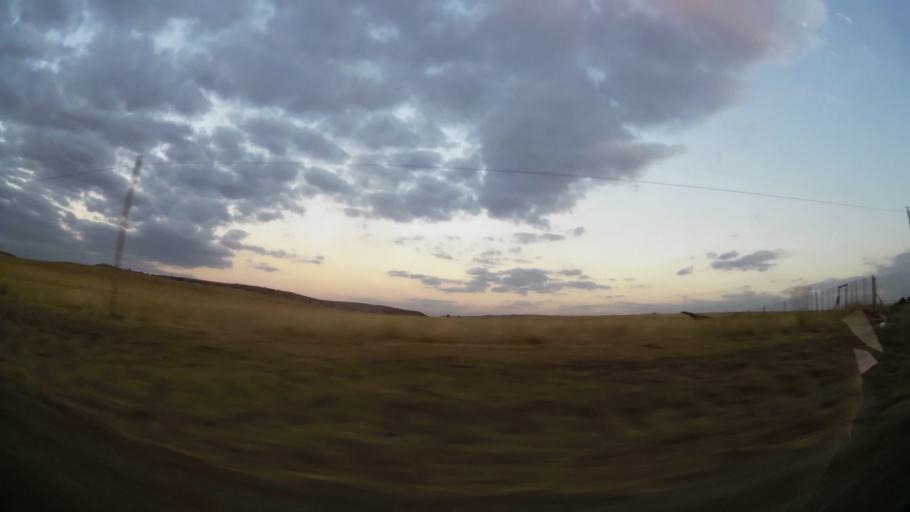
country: ZA
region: Gauteng
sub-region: West Rand District Municipality
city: Krugersdorp
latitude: -26.0537
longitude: 27.7088
